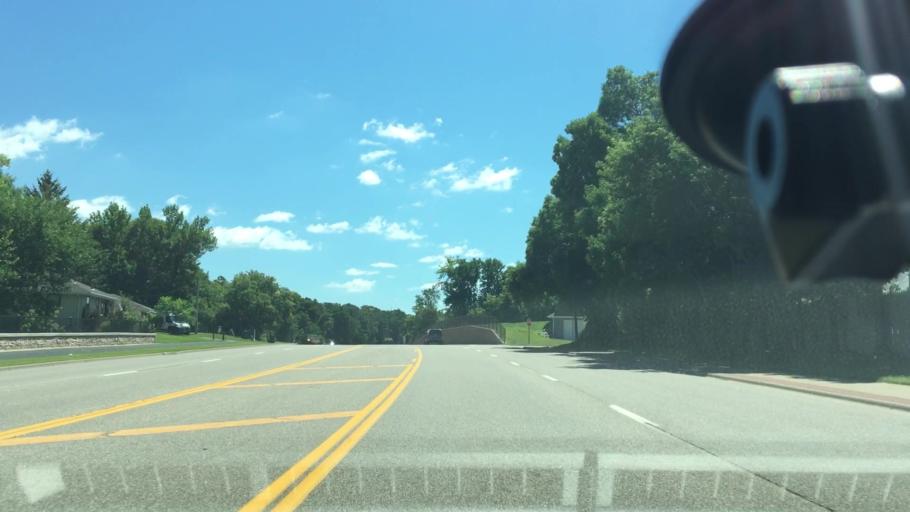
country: US
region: Minnesota
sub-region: Hennepin County
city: Maple Grove
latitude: 45.0738
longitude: -93.4592
